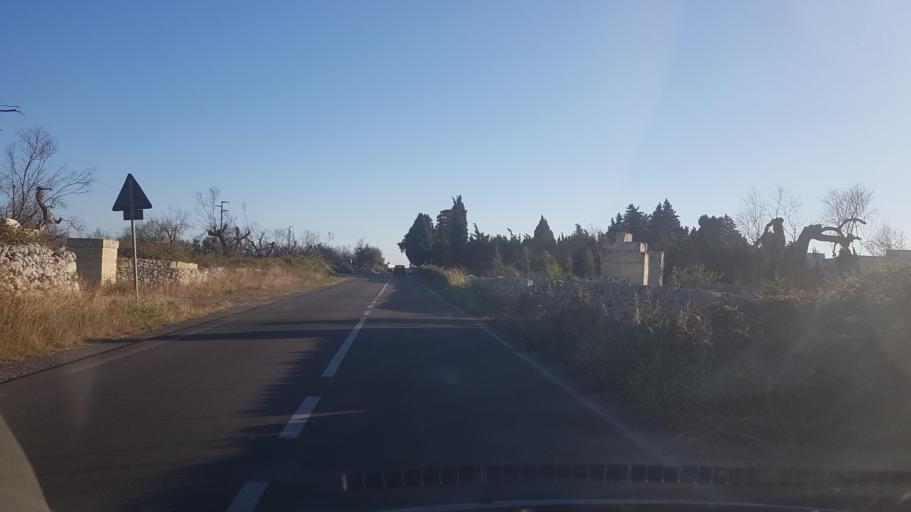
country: IT
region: Apulia
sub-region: Provincia di Lecce
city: Struda
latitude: 40.3280
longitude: 18.2893
